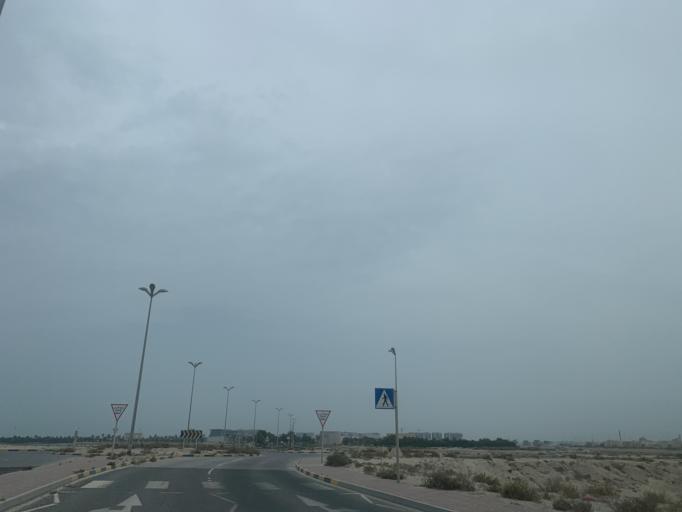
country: BH
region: Muharraq
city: Al Hadd
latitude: 26.2835
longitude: 50.6545
